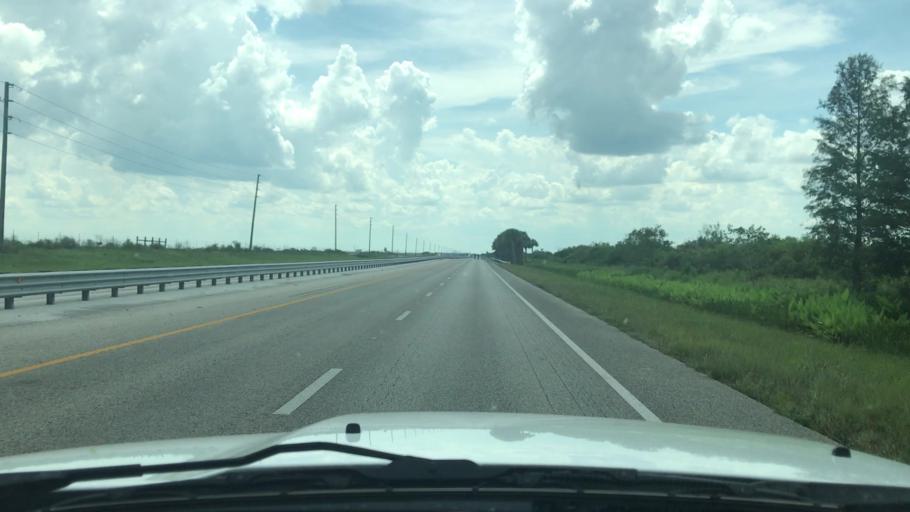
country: US
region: Florida
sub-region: Indian River County
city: Fellsmere
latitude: 27.6418
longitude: -80.7228
